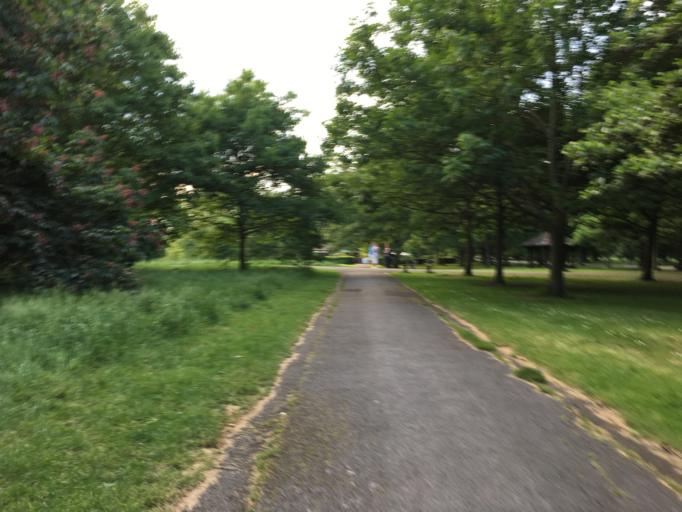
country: GB
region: England
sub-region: Greater London
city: Camden Town
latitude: 51.5300
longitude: -0.1498
